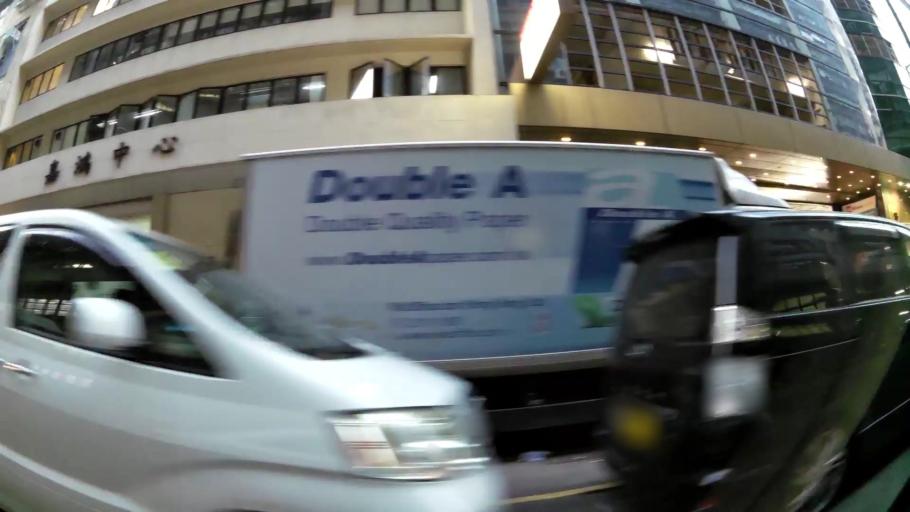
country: HK
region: Kowloon City
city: Kowloon
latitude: 22.3113
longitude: 114.2214
